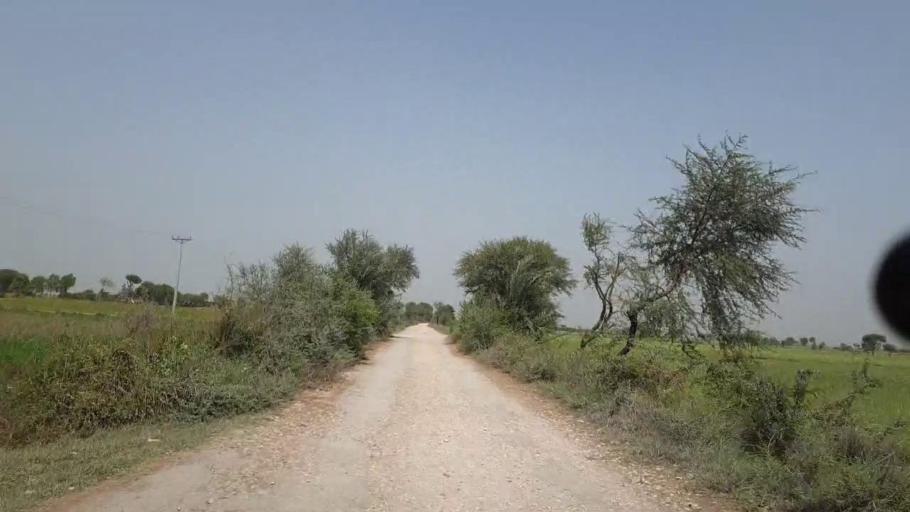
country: PK
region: Sindh
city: Matli
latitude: 25.0597
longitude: 68.6923
